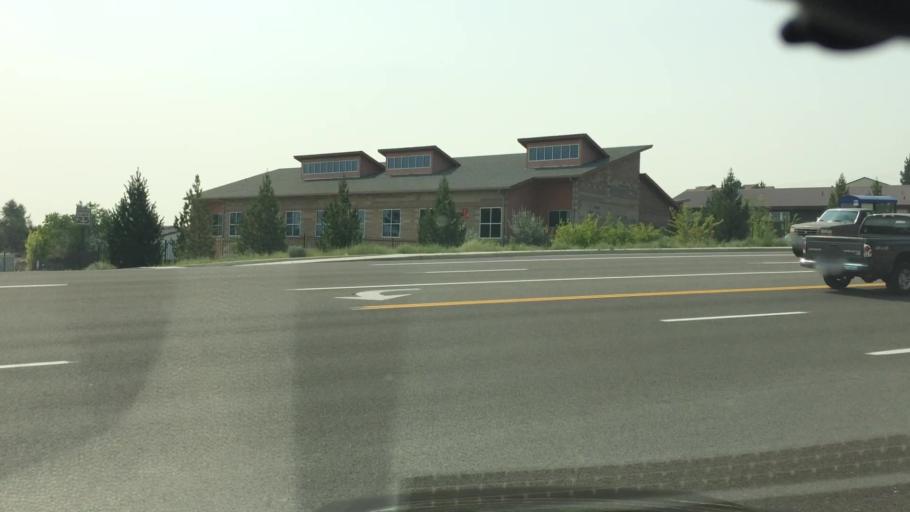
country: US
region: Nevada
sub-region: Washoe County
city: Sun Valley
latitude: 39.5668
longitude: -119.7830
